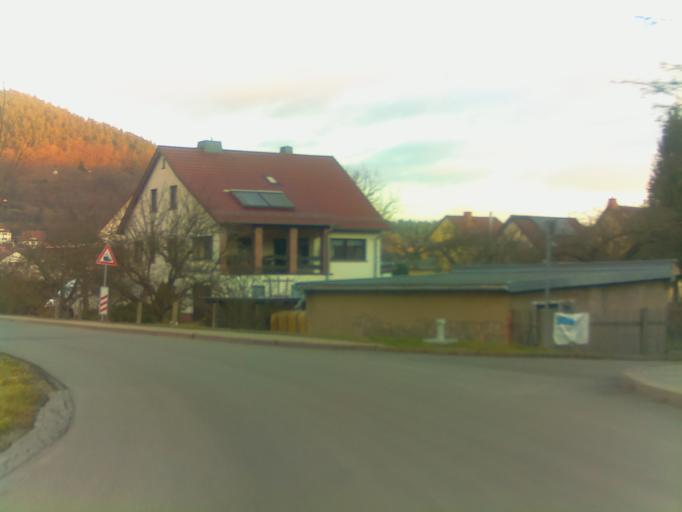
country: DE
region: Thuringia
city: Orlamunde
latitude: 50.7381
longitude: 11.4677
